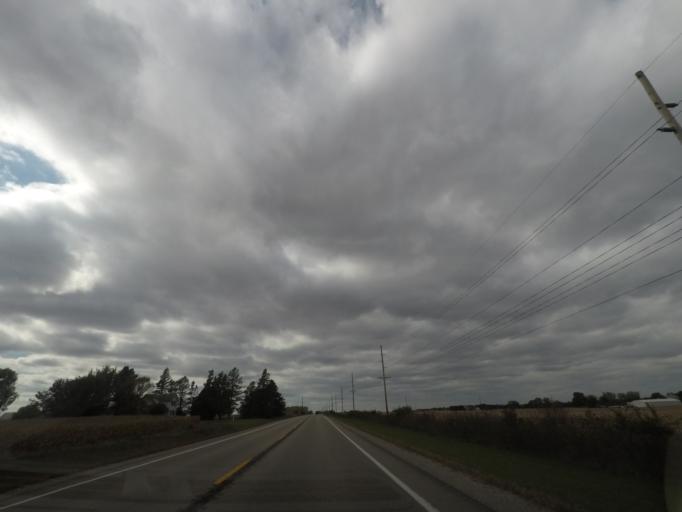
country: US
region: Iowa
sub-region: Story County
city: Huxley
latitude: 41.8778
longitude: -93.5534
